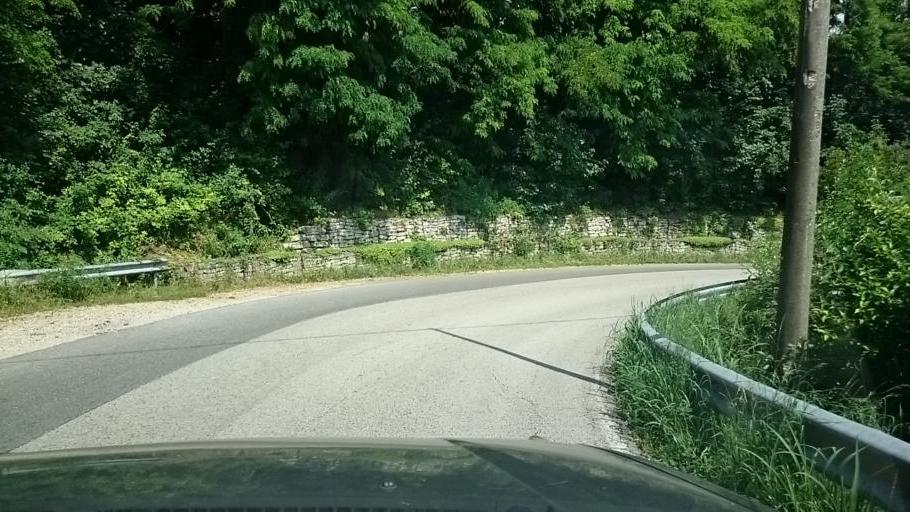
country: IT
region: Veneto
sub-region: Provincia di Vicenza
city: Conco
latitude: 45.7739
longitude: 11.6164
